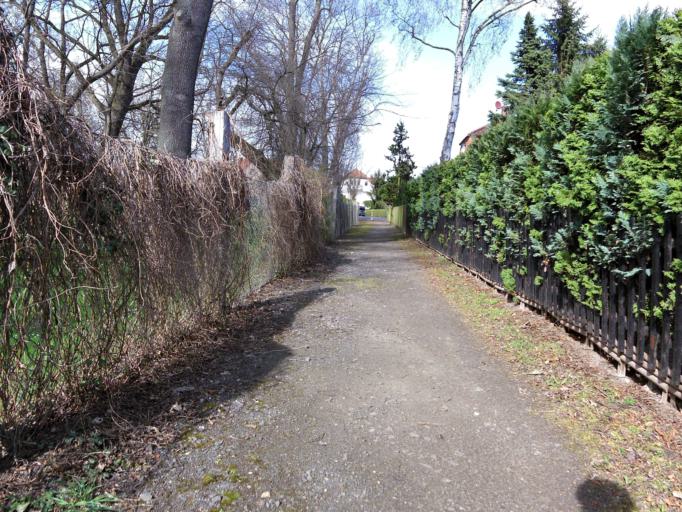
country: DE
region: Saxony
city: Schkeuditz
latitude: 51.3801
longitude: 12.2763
